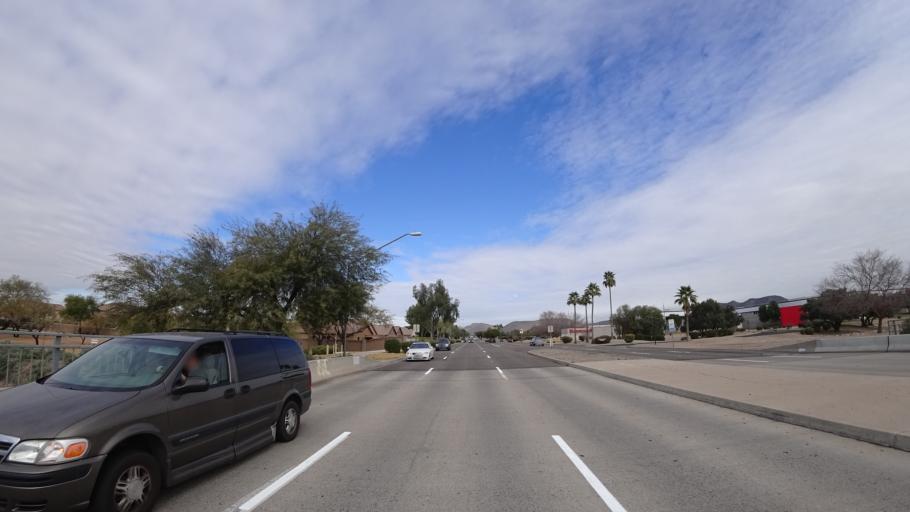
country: US
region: Arizona
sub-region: Maricopa County
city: Peoria
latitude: 33.6557
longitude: -112.1864
